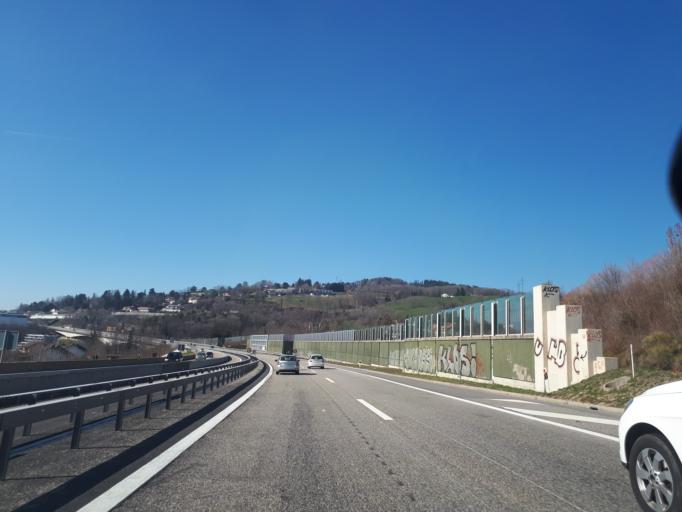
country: CH
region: Vaud
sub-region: Lavaux-Oron District
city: Lutry
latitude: 46.5129
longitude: 6.7017
